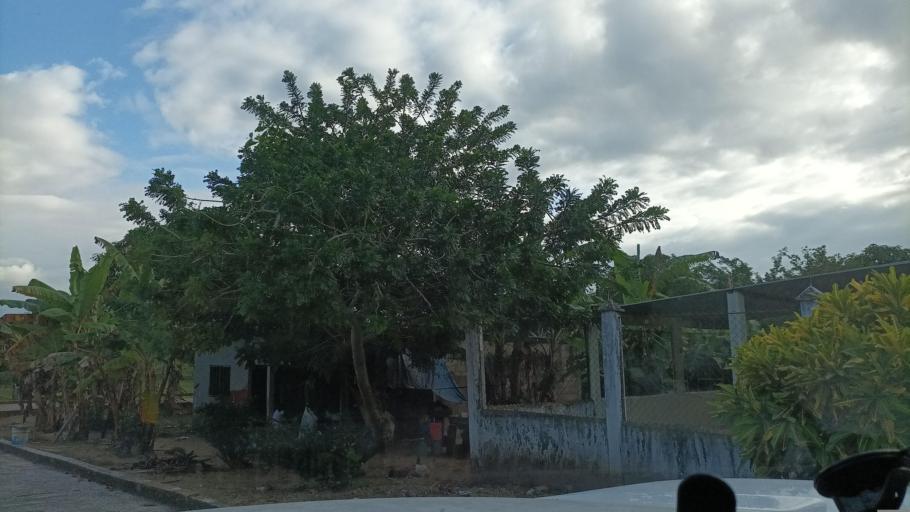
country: MX
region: Veracruz
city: Oluta
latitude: 17.8922
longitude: -94.8680
